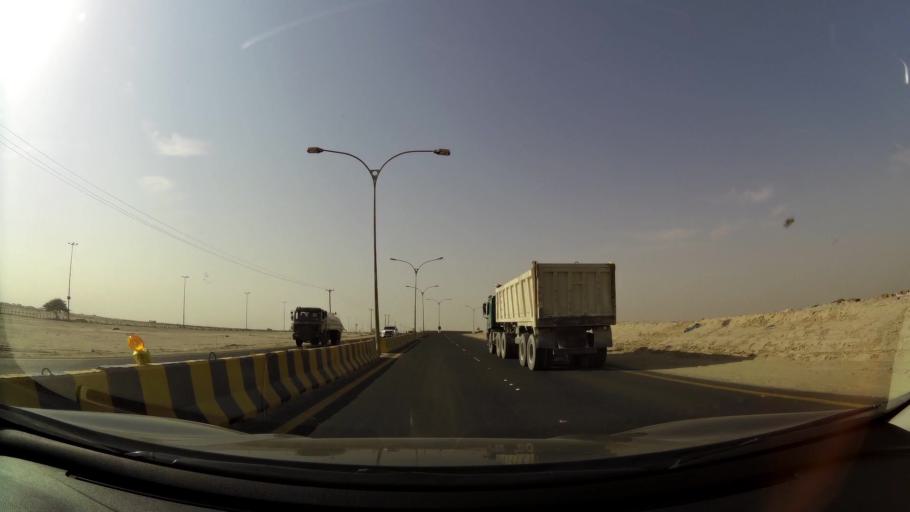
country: KW
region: Al Ahmadi
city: Al Ahmadi
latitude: 28.8973
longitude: 48.0883
